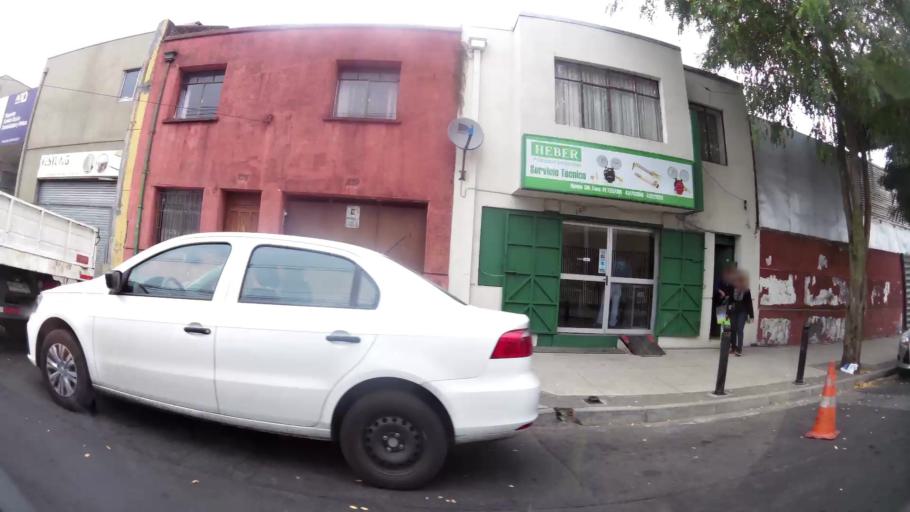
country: CL
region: Biobio
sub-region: Provincia de Concepcion
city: Concepcion
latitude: -36.8232
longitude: -73.0609
